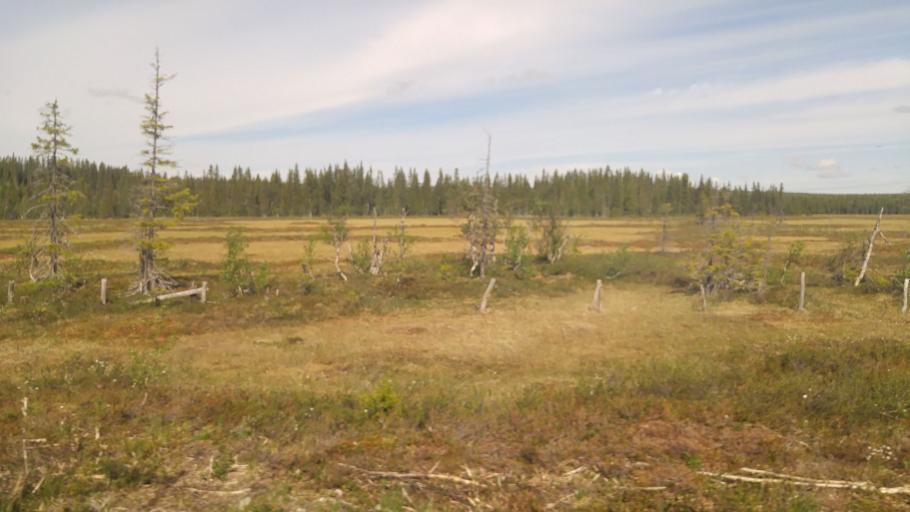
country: SE
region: Jaemtland
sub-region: Are Kommun
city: Are
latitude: 63.3300
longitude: 12.5673
